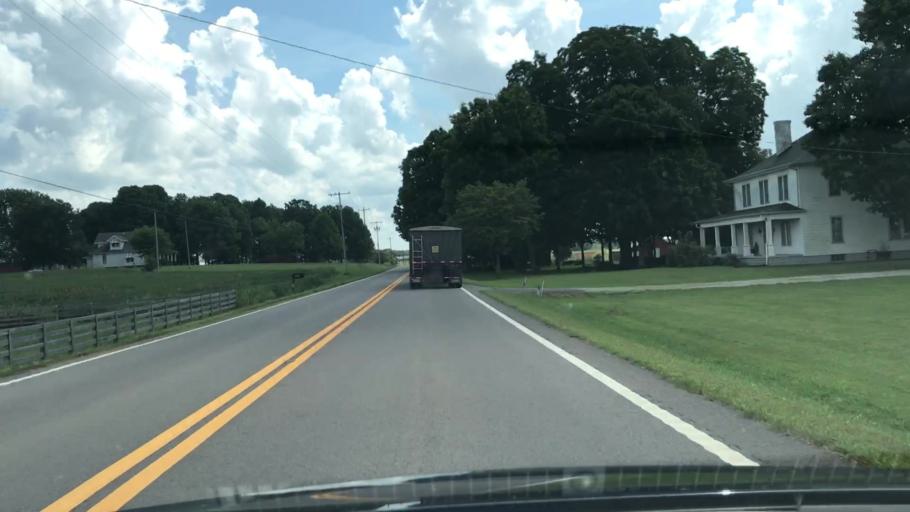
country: US
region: Tennessee
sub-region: Robertson County
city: Springfield
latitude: 36.6073
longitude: -86.9276
